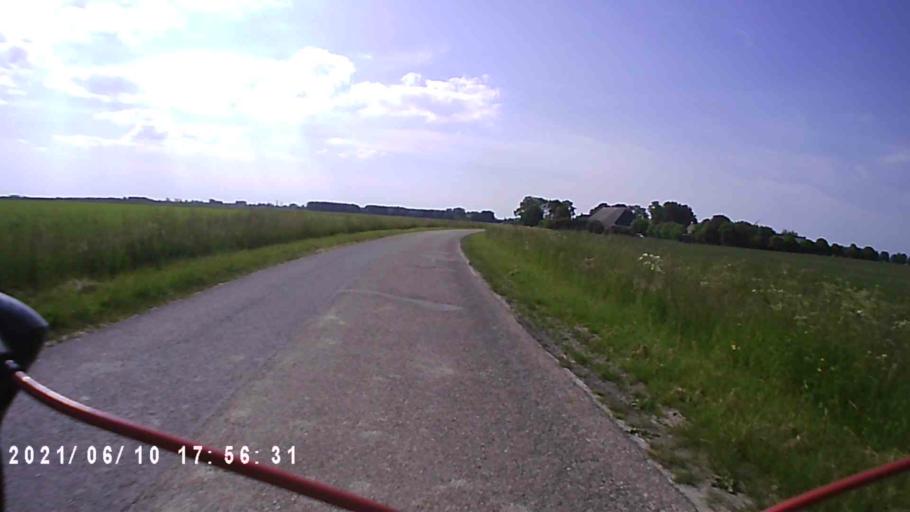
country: NL
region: Groningen
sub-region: Gemeente De Marne
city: Ulrum
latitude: 53.3309
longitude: 6.3313
